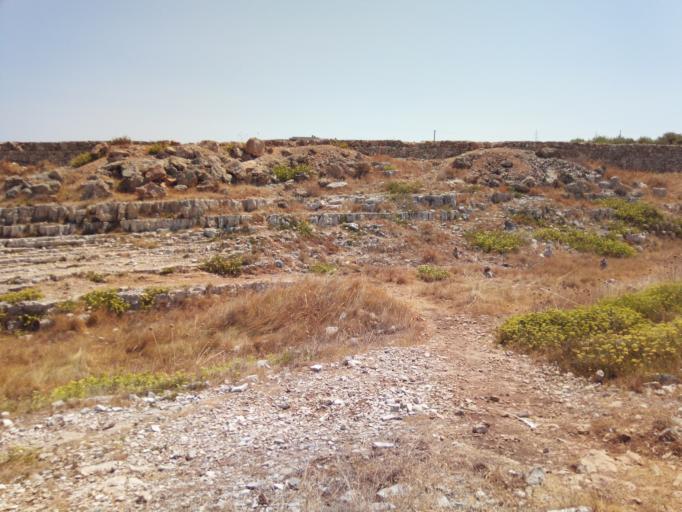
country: IT
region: Apulia
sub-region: Provincia di Bari
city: Polignano a Mare
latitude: 40.9920
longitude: 17.2341
